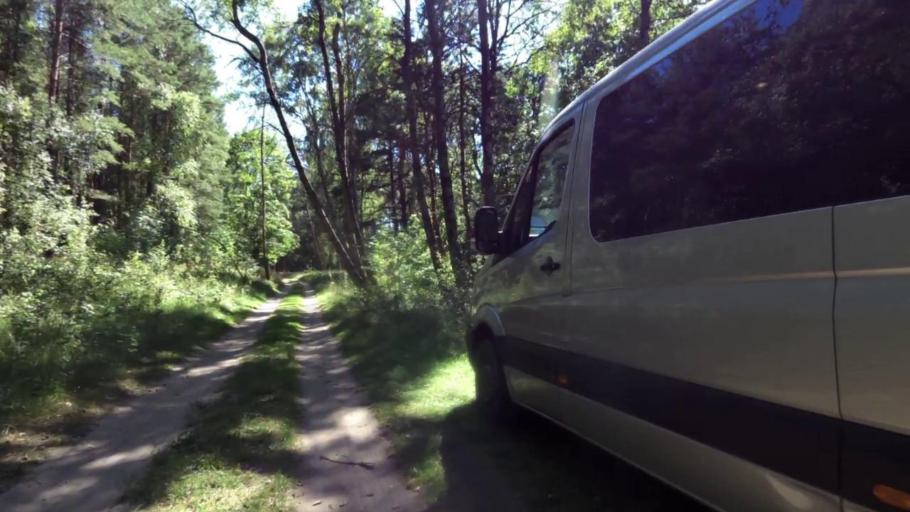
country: PL
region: West Pomeranian Voivodeship
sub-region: Powiat szczecinecki
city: Bialy Bor
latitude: 53.8496
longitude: 16.8704
